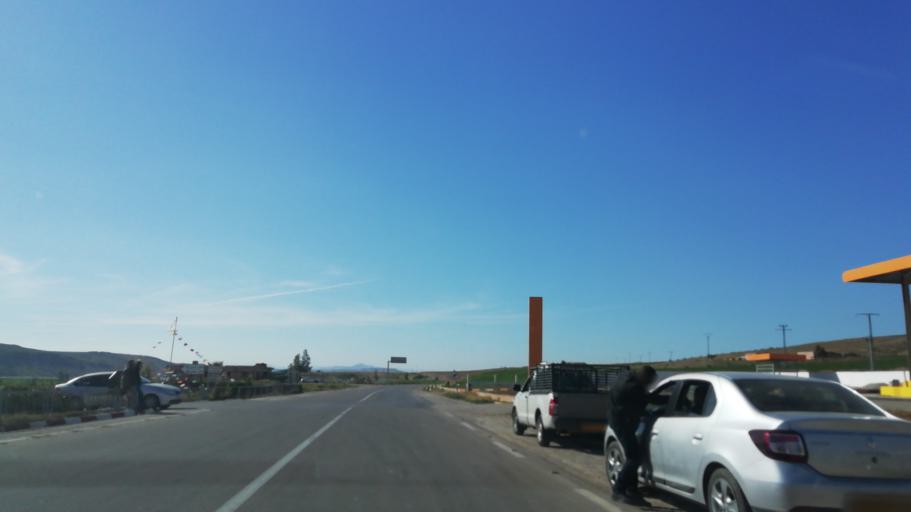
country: DZ
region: Mascara
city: Oued el Abtal
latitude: 35.4511
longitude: 0.7813
